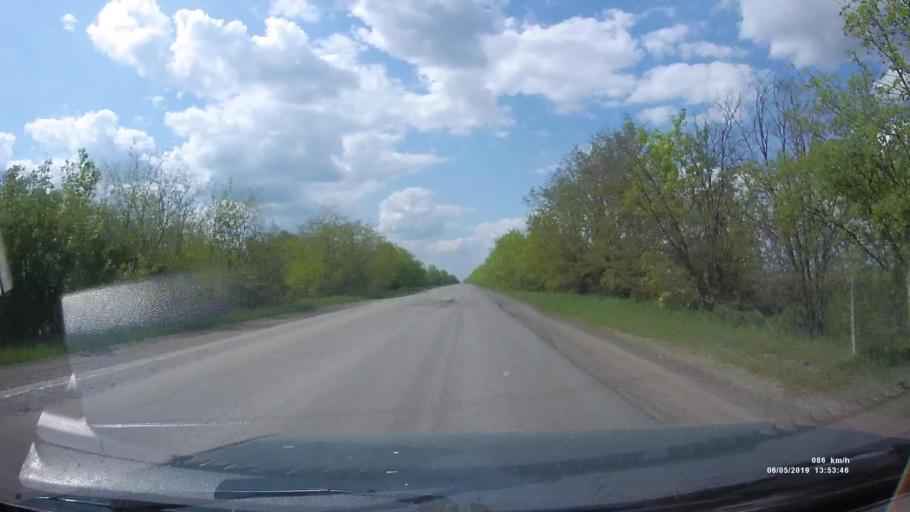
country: RU
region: Rostov
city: Melikhovskaya
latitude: 47.6703
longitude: 40.4573
